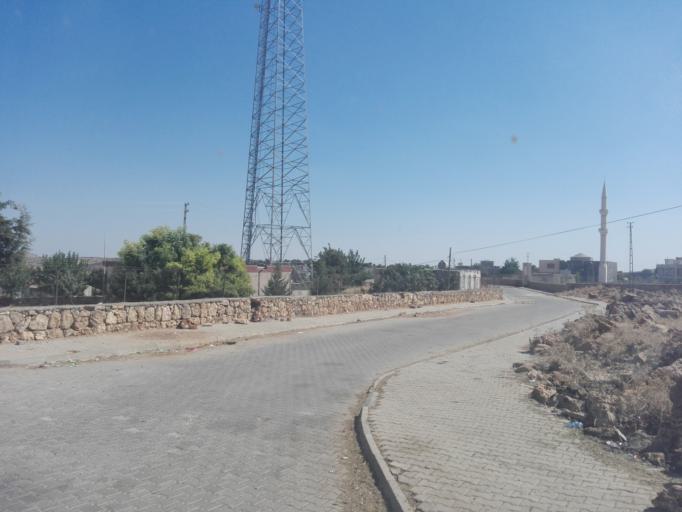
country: TR
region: Mardin
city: Kilavuz
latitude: 37.4825
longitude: 41.7766
